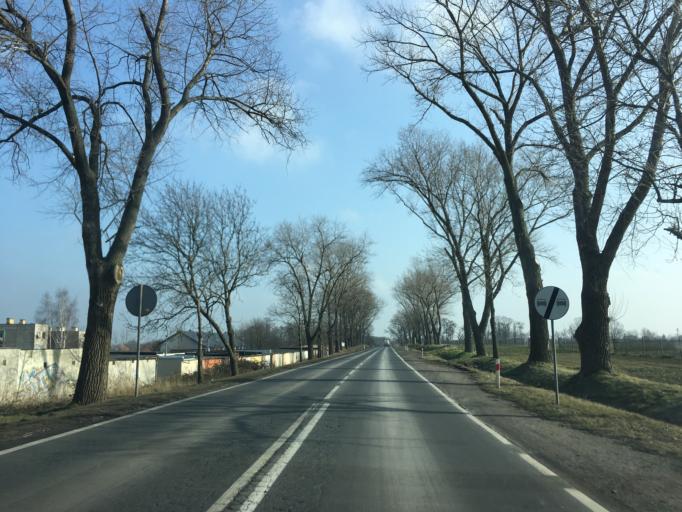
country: PL
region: Lower Silesian Voivodeship
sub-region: Powiat legnicki
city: Chojnow
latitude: 51.2652
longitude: 15.9419
